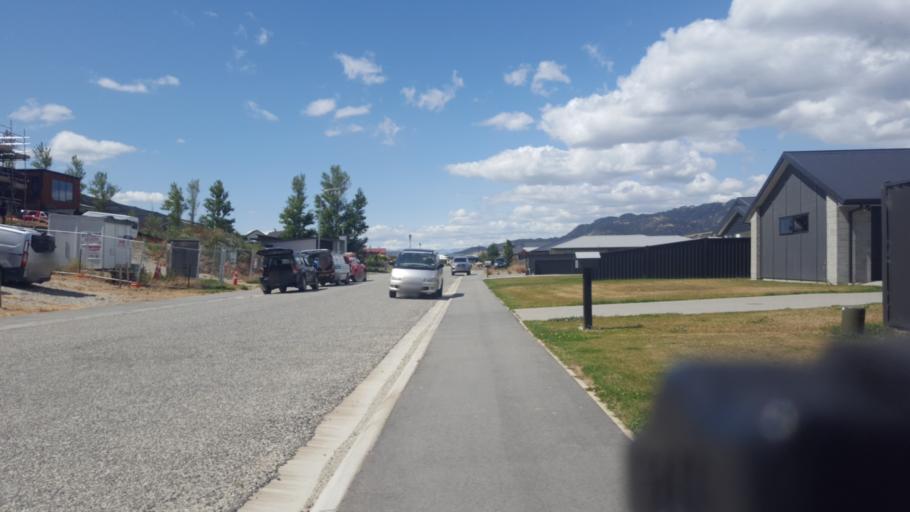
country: NZ
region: Otago
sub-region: Queenstown-Lakes District
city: Wanaka
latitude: -44.9741
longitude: 169.2418
